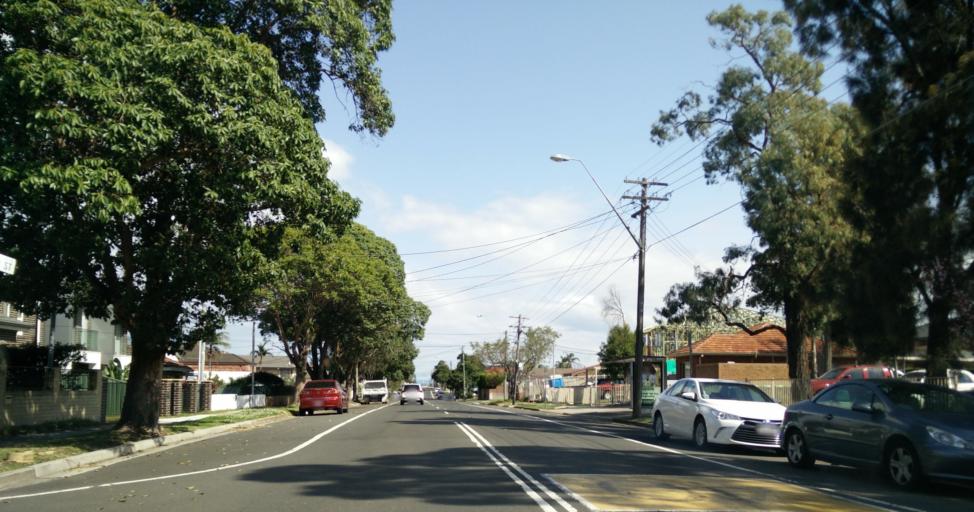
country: AU
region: New South Wales
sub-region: Bankstown
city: Revesby
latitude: -33.9572
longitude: 151.0063
